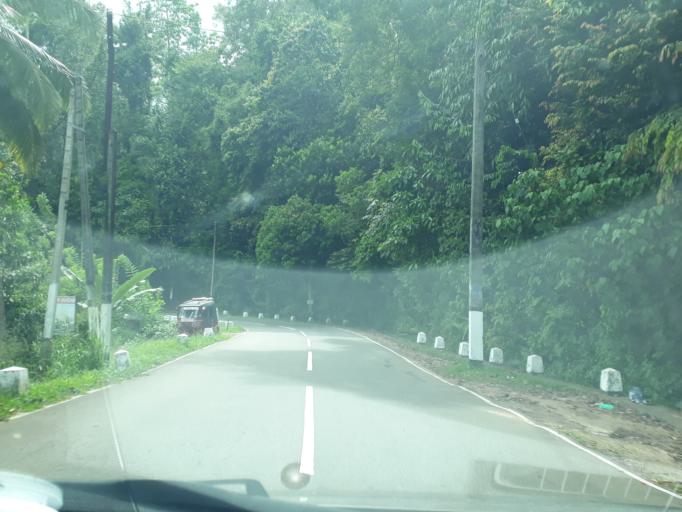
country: LK
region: Southern
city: Weligama
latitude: 6.3160
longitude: 80.5438
